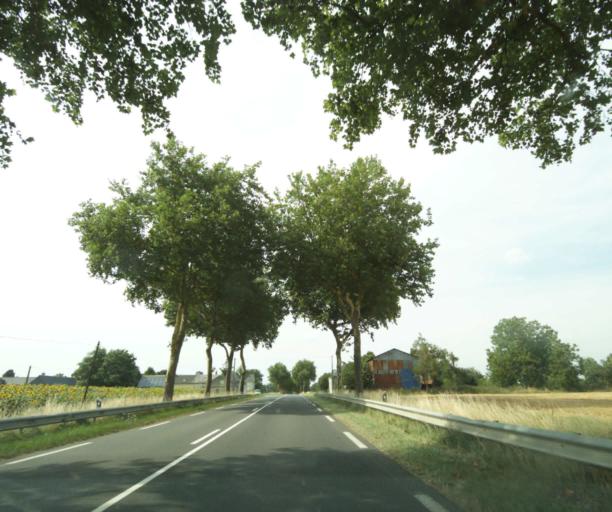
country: FR
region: Centre
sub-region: Departement d'Indre-et-Loire
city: Neuille-Pont-Pierre
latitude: 47.5719
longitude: 0.5460
